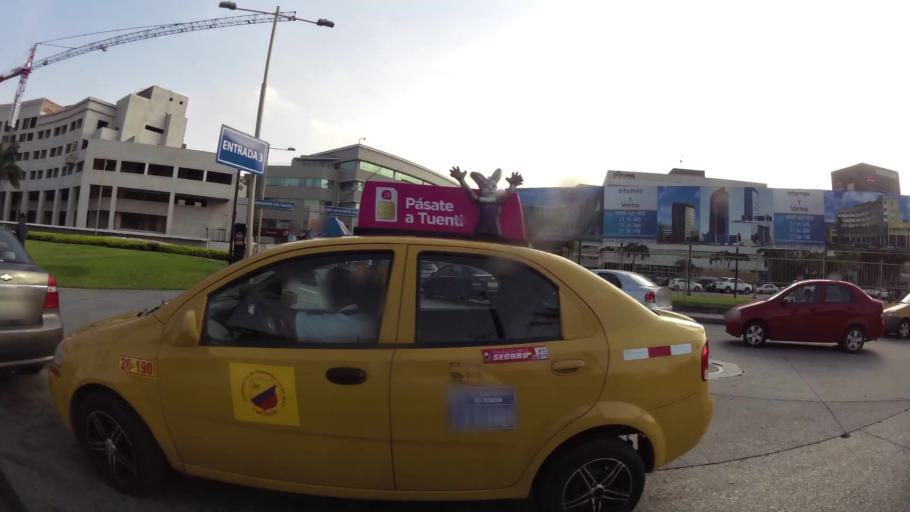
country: EC
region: Guayas
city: Guayaquil
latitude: -2.1511
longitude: -79.9056
